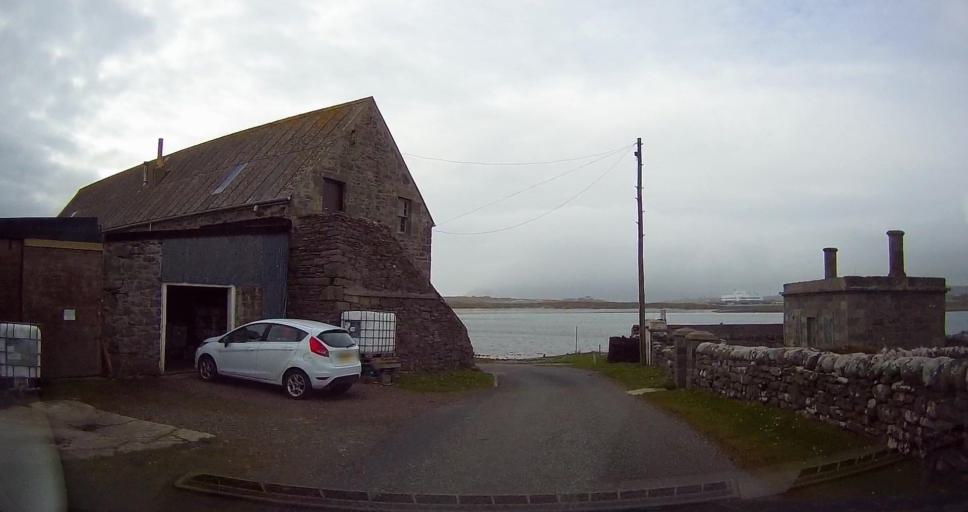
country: GB
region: Scotland
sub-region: Shetland Islands
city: Sandwick
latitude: 59.8725
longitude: -1.2782
